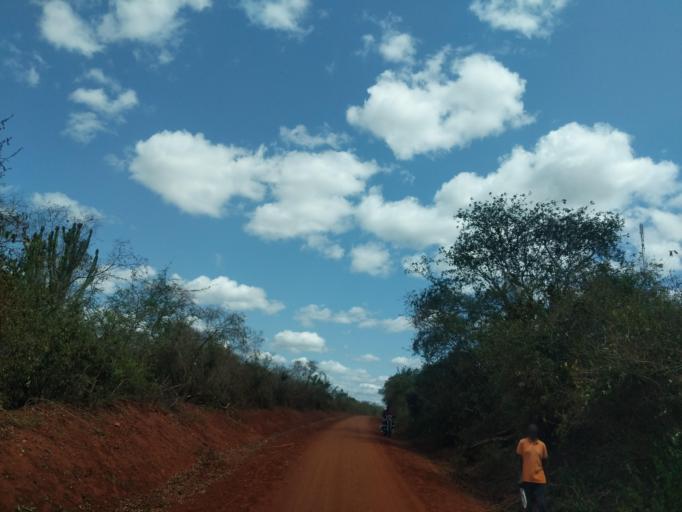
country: TZ
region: Tanga
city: Chanika
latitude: -5.5167
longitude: 38.3545
